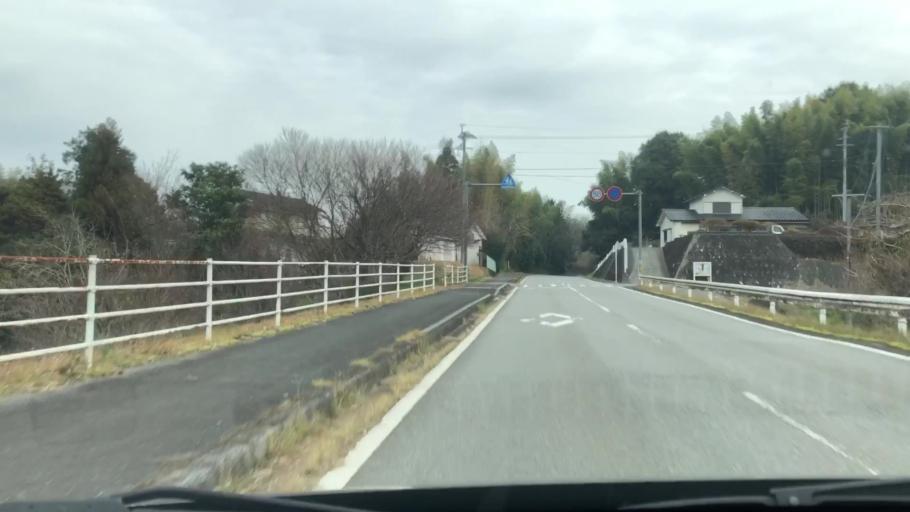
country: JP
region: Oita
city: Usuki
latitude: 33.0151
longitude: 131.6668
